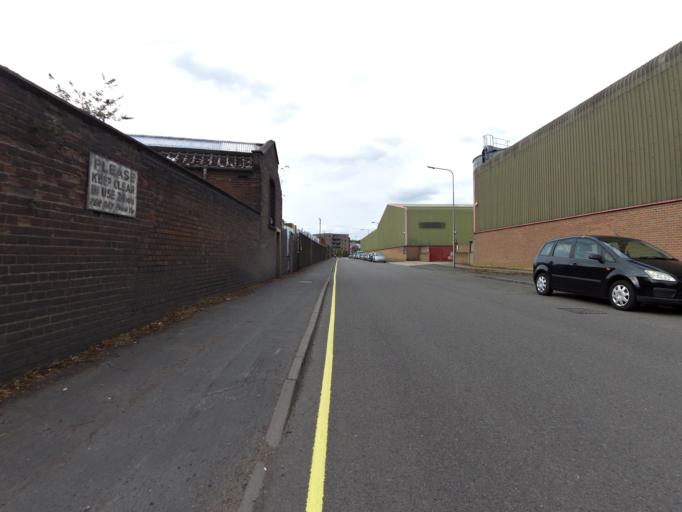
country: GB
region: England
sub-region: Suffolk
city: Ipswich
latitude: 52.0468
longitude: 1.1651
